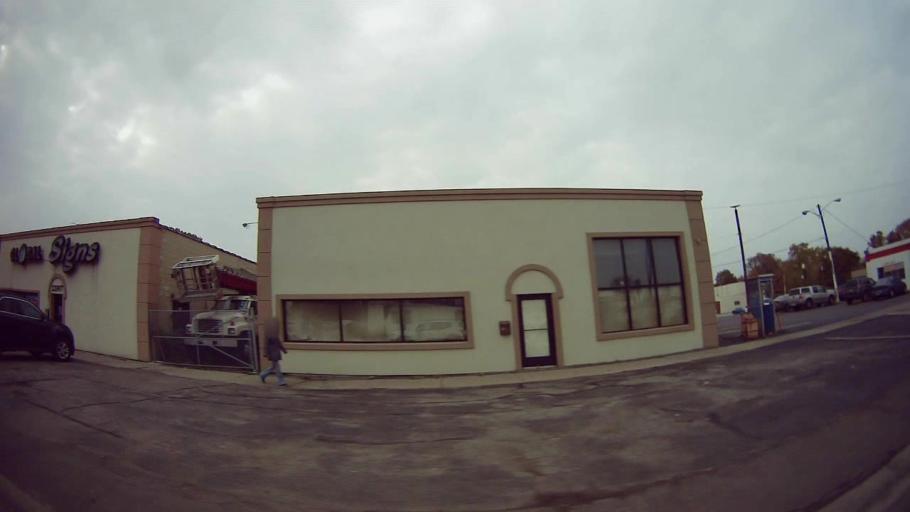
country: US
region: Michigan
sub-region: Oakland County
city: Hazel Park
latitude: 42.4603
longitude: -83.0840
